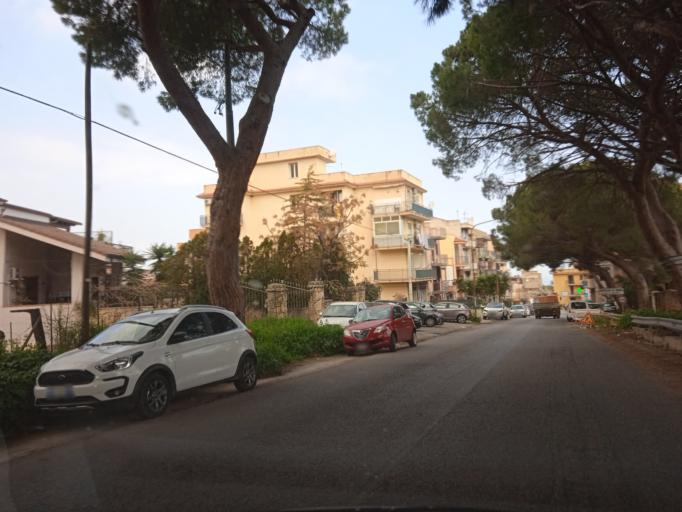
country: IT
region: Sicily
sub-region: Palermo
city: Portella di Mare
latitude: 38.0678
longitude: 13.4588
